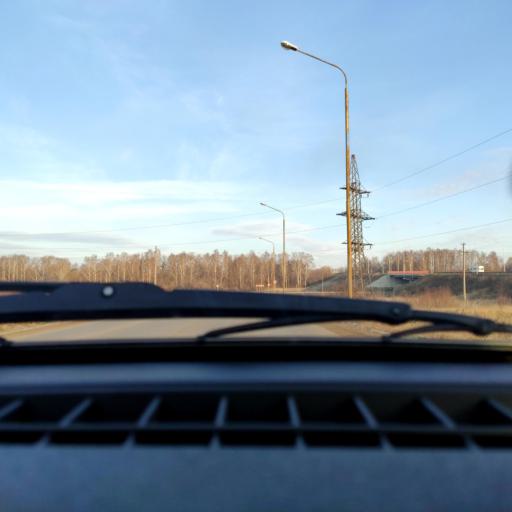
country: RU
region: Bashkortostan
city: Iglino
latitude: 54.7704
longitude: 56.2583
